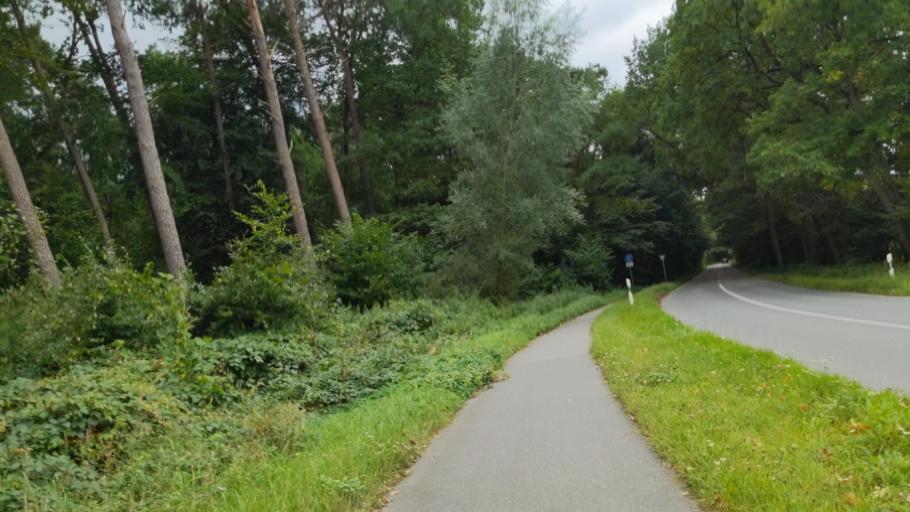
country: DE
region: Schleswig-Holstein
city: Klempau
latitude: 53.7909
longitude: 10.6991
